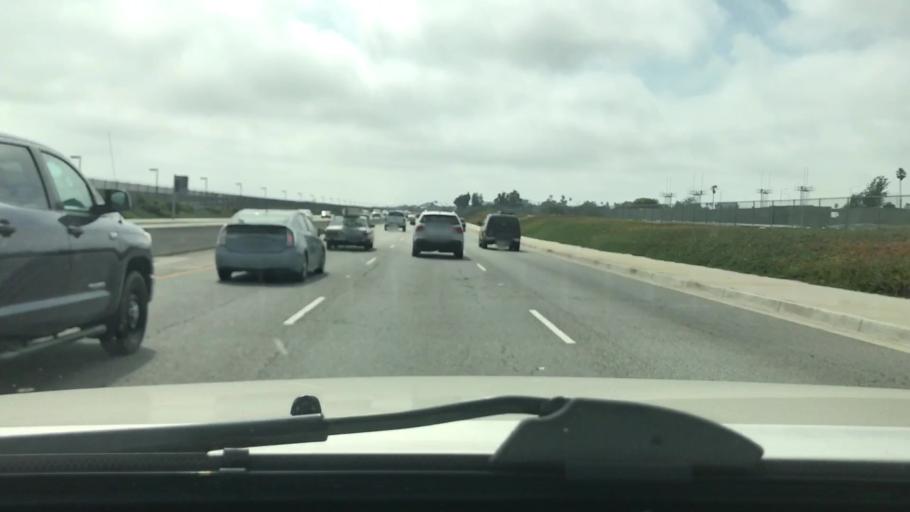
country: US
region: California
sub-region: Los Angeles County
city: El Segundo
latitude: 33.9534
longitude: -118.3991
